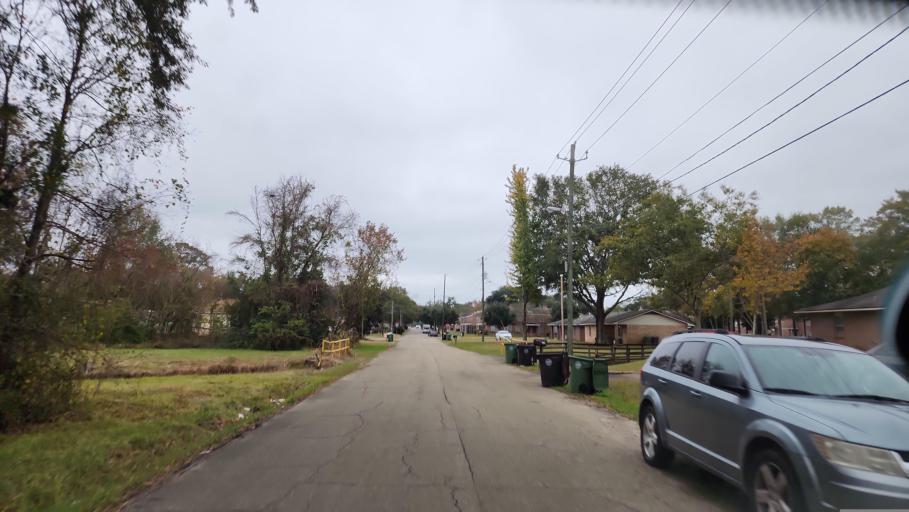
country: US
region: Mississippi
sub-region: Forrest County
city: Hattiesburg
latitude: 31.3170
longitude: -89.2947
